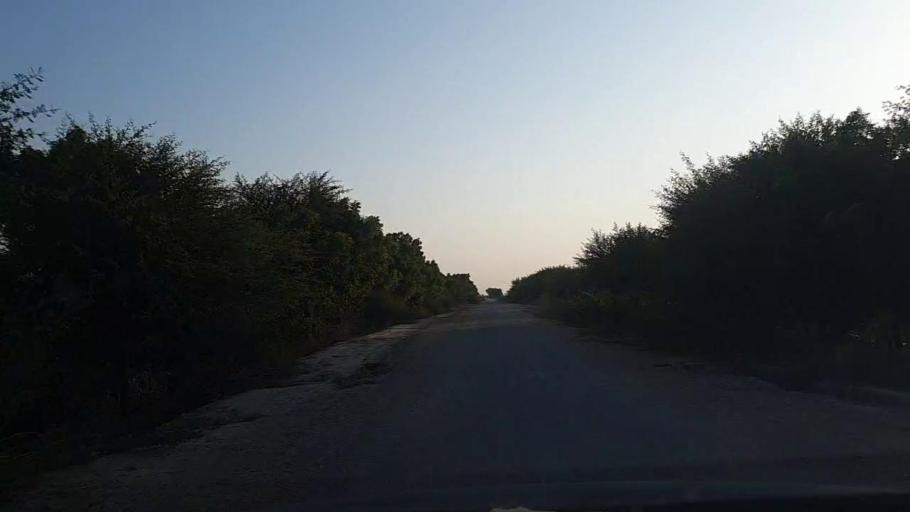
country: PK
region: Sindh
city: Naukot
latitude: 24.8409
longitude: 69.3117
